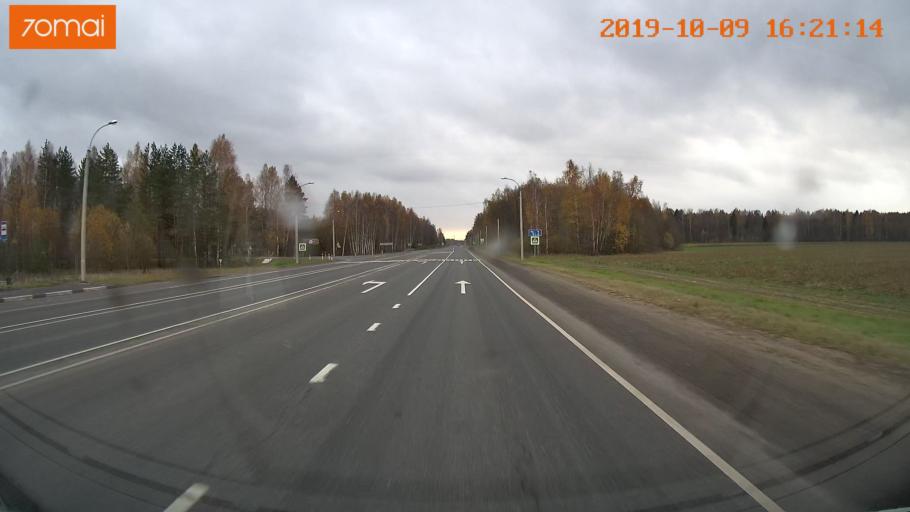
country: RU
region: Kostroma
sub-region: Kostromskoy Rayon
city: Kostroma
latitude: 57.6951
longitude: 40.8898
